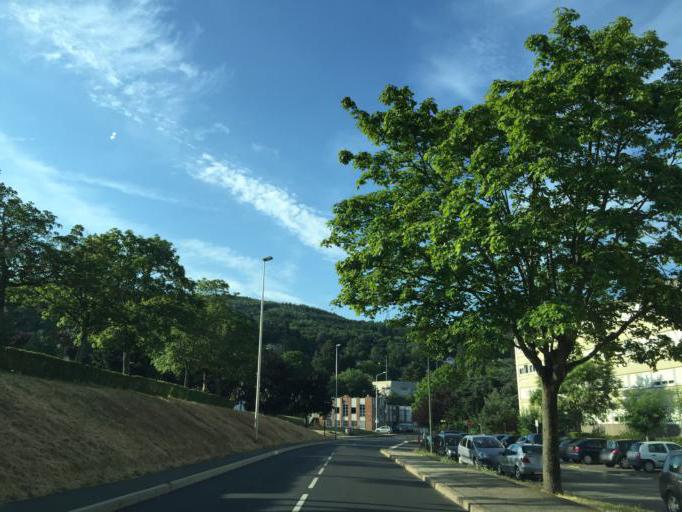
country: FR
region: Rhone-Alpes
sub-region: Departement de la Loire
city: Saint-Etienne
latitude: 45.4224
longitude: 4.4254
